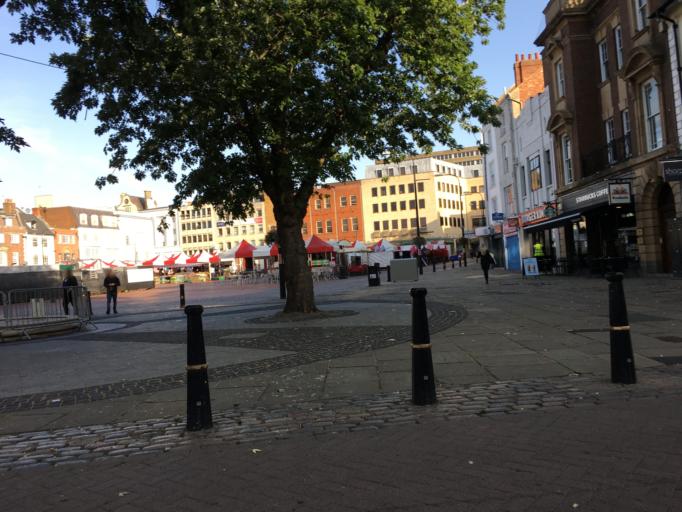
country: GB
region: England
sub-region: Northamptonshire
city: Northampton
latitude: 52.2376
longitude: -0.8957
